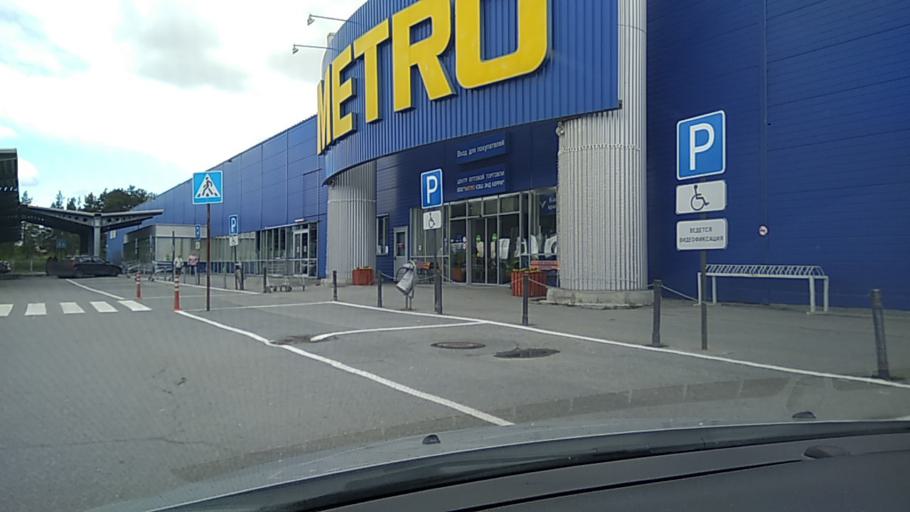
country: RU
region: Sverdlovsk
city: Istok
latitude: 56.8230
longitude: 60.7137
